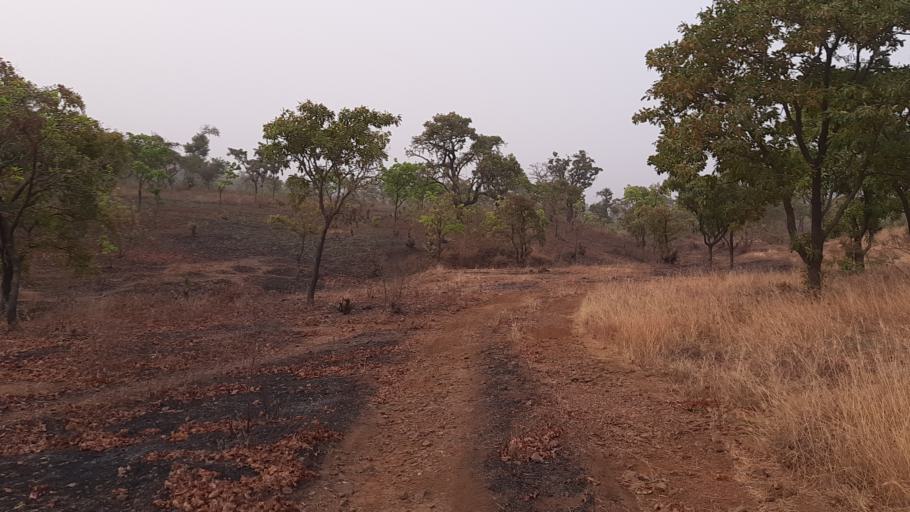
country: GH
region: Upper East
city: Bolgatanga
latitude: 10.7890
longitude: -0.7574
